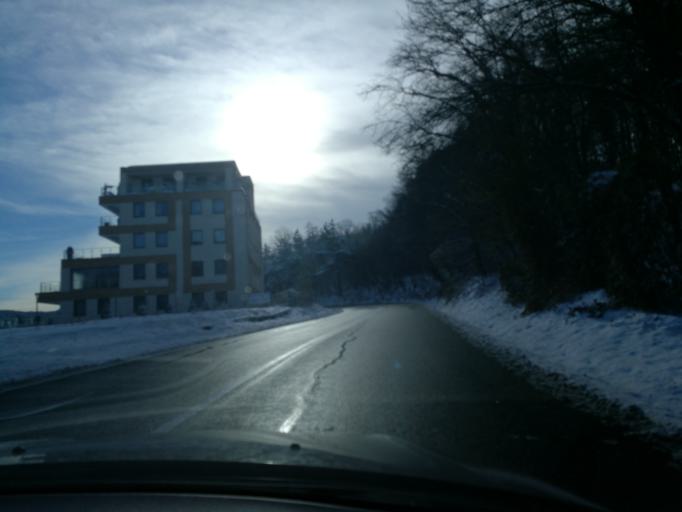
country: RO
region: Brasov
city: Brasov
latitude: 45.6392
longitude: 25.5631
